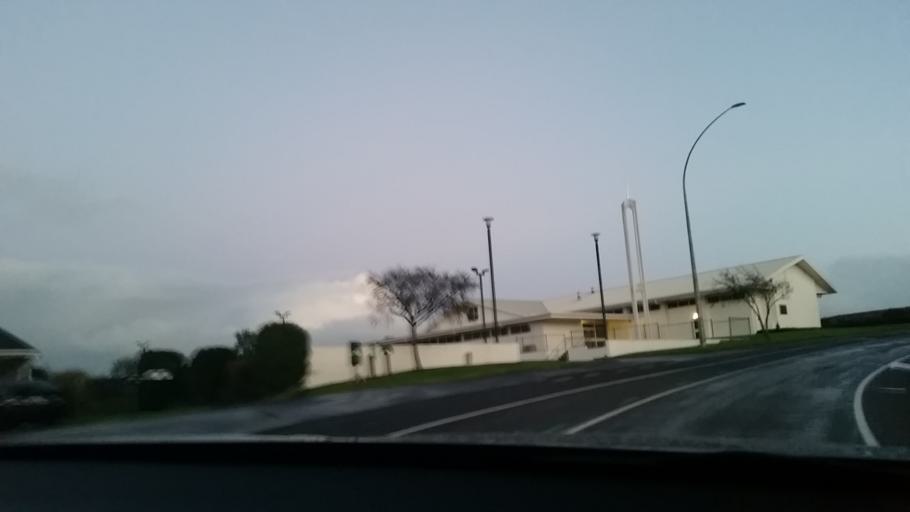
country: NZ
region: Waikato
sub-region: Hamilton City
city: Hamilton
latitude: -37.7990
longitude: 175.2481
